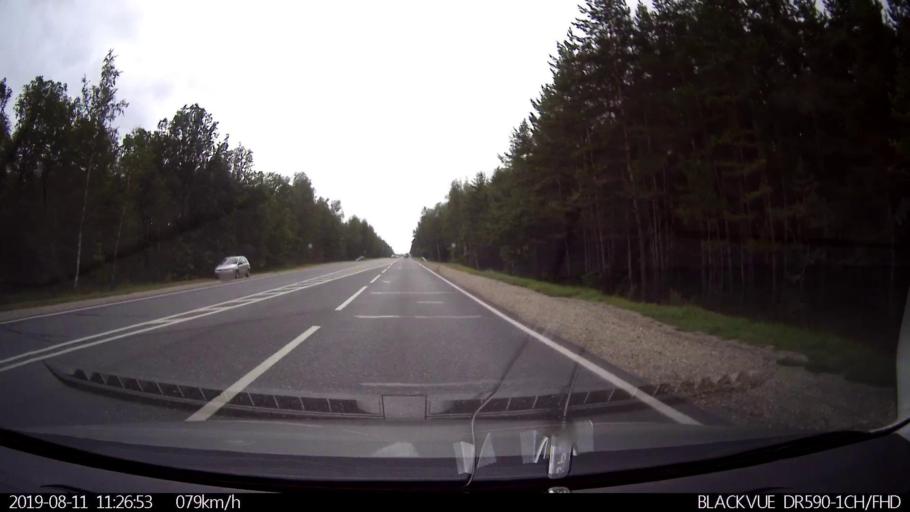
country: RU
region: Ulyanovsk
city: Krasnyy Gulyay
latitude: 54.0999
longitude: 48.2335
